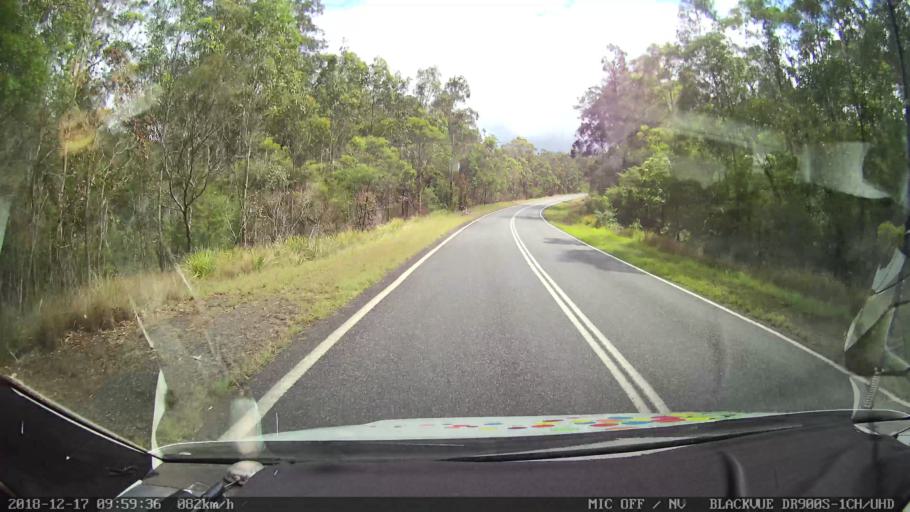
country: AU
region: New South Wales
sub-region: Tenterfield Municipality
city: Carrolls Creek
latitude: -28.9082
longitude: 152.4147
